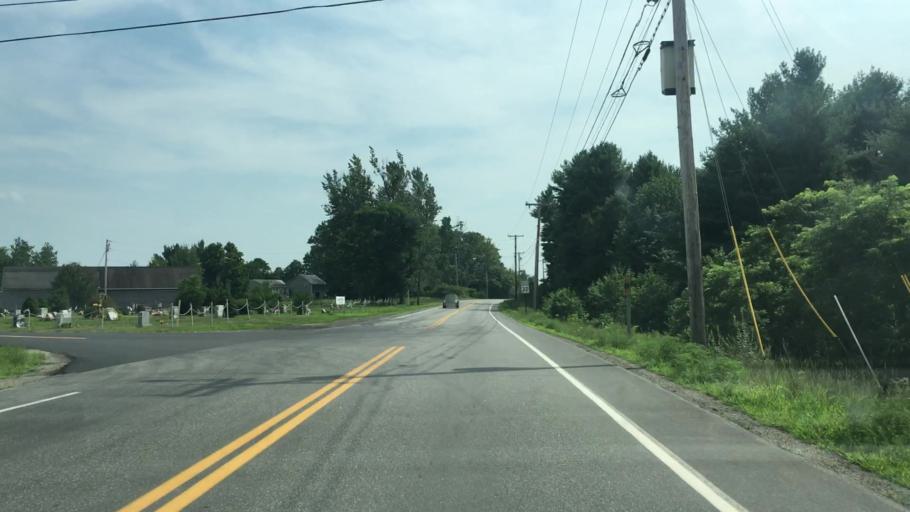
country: US
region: Maine
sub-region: Kennebec County
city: Windsor
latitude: 44.2946
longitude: -69.5853
